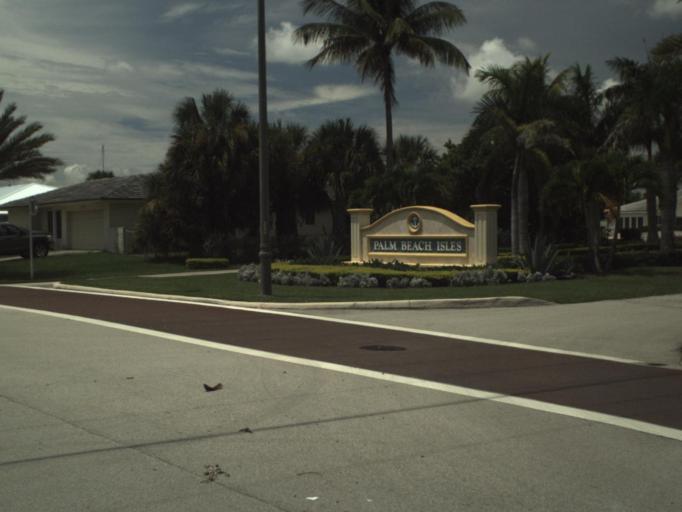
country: US
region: Florida
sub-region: Palm Beach County
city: Palm Beach Shores
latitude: 26.7945
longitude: -80.0345
